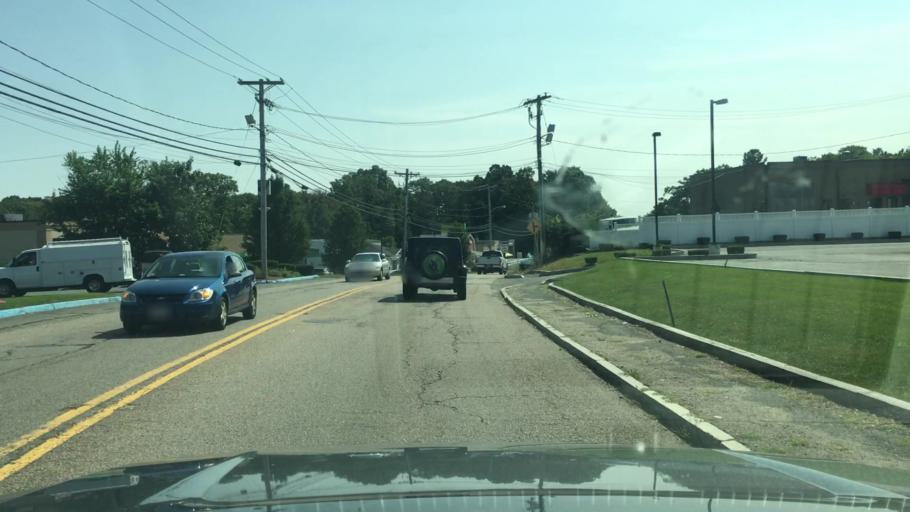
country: US
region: Massachusetts
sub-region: Plymouth County
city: Abington
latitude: 42.1381
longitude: -70.9506
